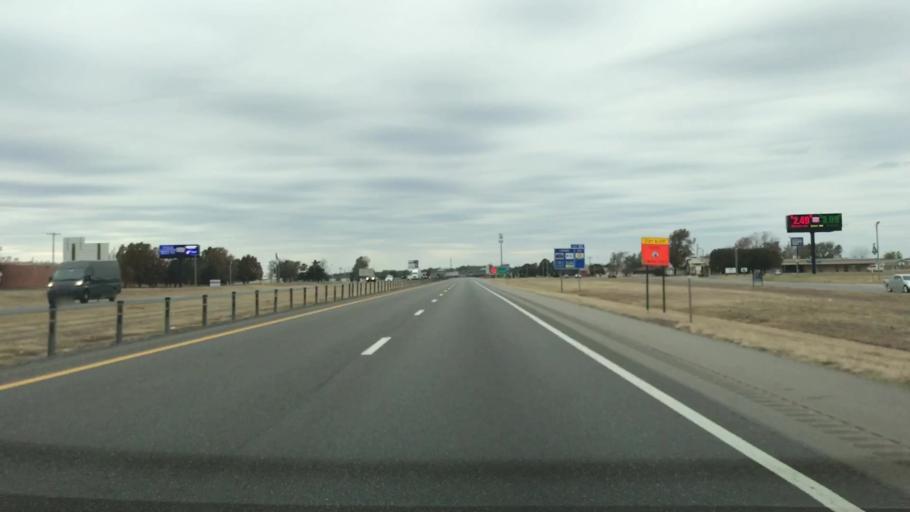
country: US
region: Oklahoma
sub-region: Custer County
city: Weatherford
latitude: 35.5365
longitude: -98.6690
